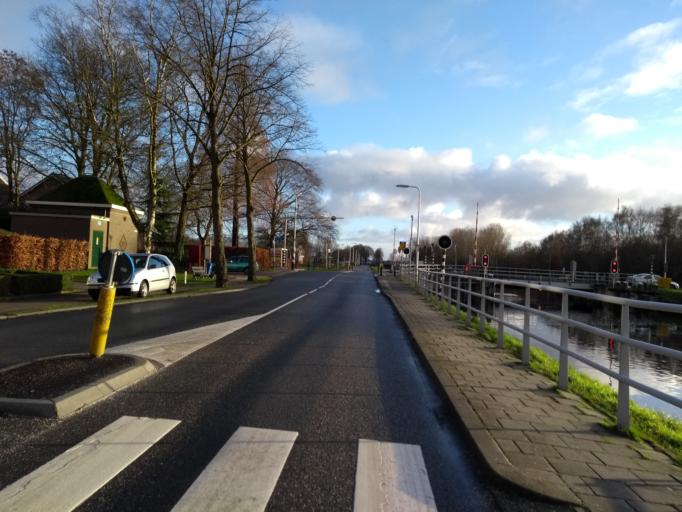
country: NL
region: Overijssel
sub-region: Gemeente Twenterand
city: Vriezenveen
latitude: 52.3755
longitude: 6.6298
